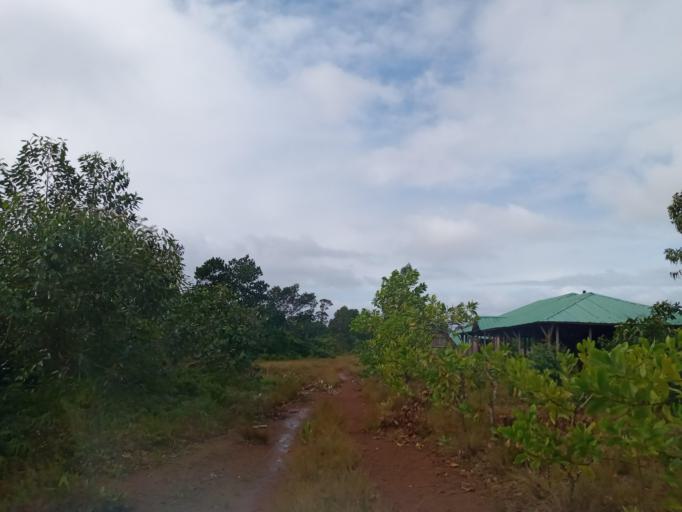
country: MG
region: Atsimo-Atsinanana
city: Vohipaho
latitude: -23.7925
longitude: 47.5492
